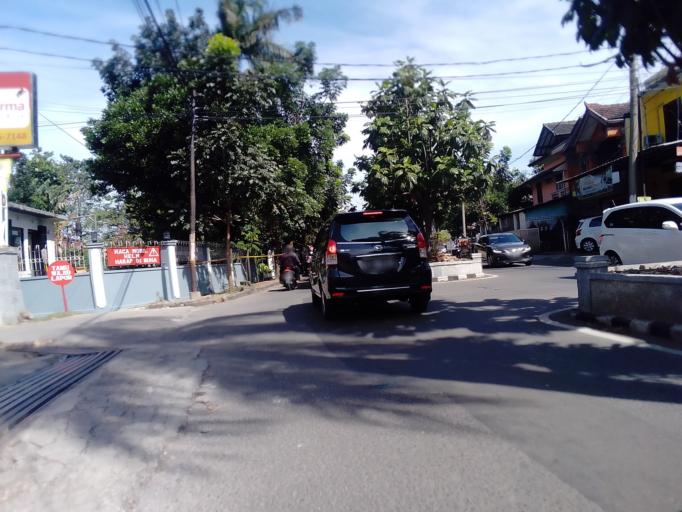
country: ID
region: West Java
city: Bandung
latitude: -6.9419
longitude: 107.6673
